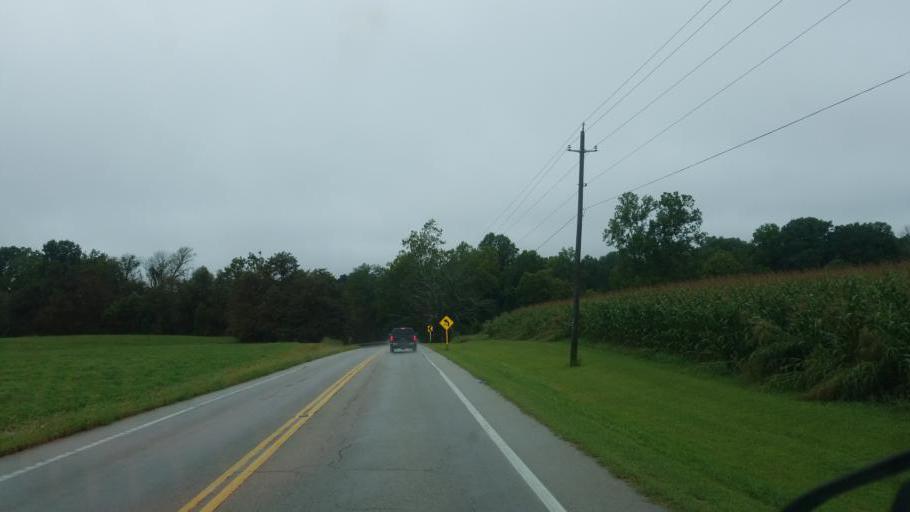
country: US
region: Ohio
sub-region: Adams County
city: West Union
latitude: 38.7983
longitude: -83.5036
